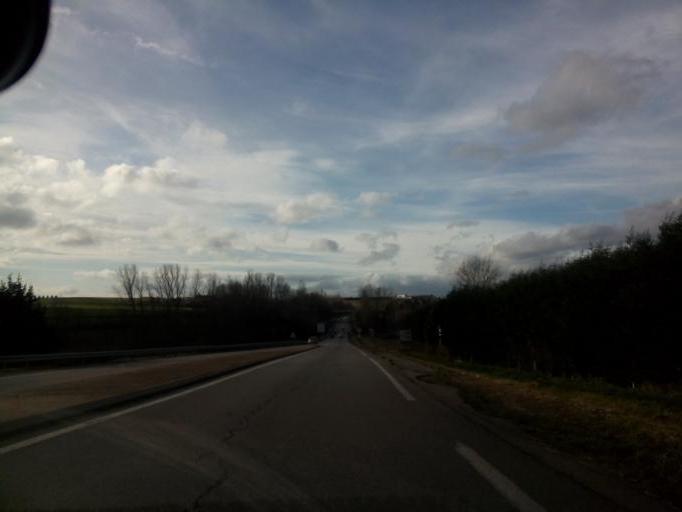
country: FR
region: Rhone-Alpes
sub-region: Departement de l'Ardeche
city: Peaugres
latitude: 45.2908
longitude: 4.7346
